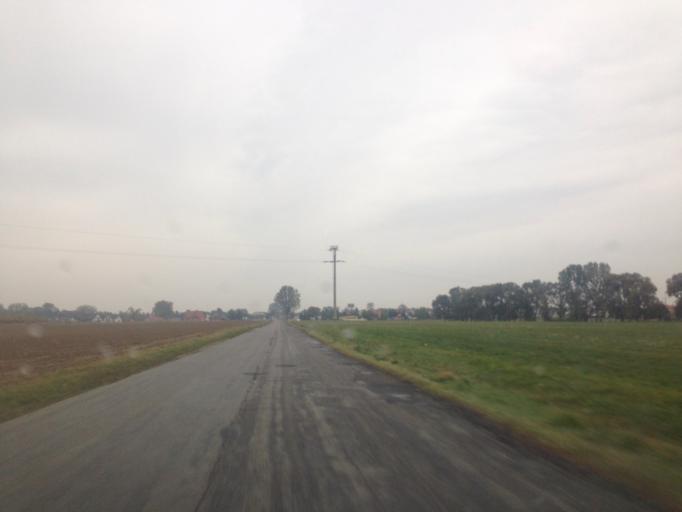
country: PL
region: Greater Poland Voivodeship
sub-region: Powiat poznanski
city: Kleszczewo
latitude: 52.3566
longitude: 17.1386
